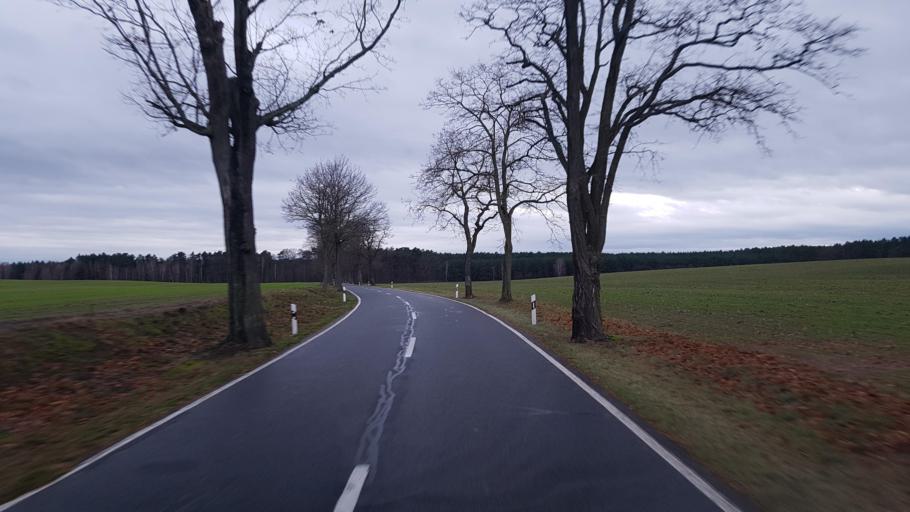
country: DE
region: Brandenburg
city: Schlepzig
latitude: 52.0619
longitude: 14.0233
